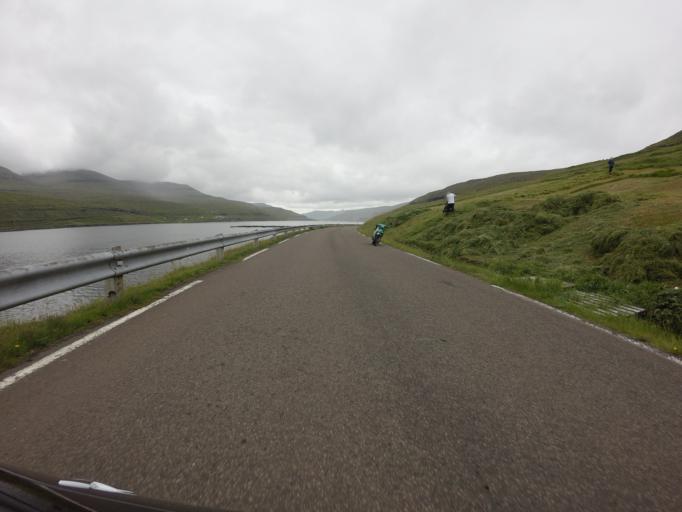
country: FO
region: Eysturoy
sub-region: Eidi
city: Eidi
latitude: 62.2799
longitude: -7.0906
